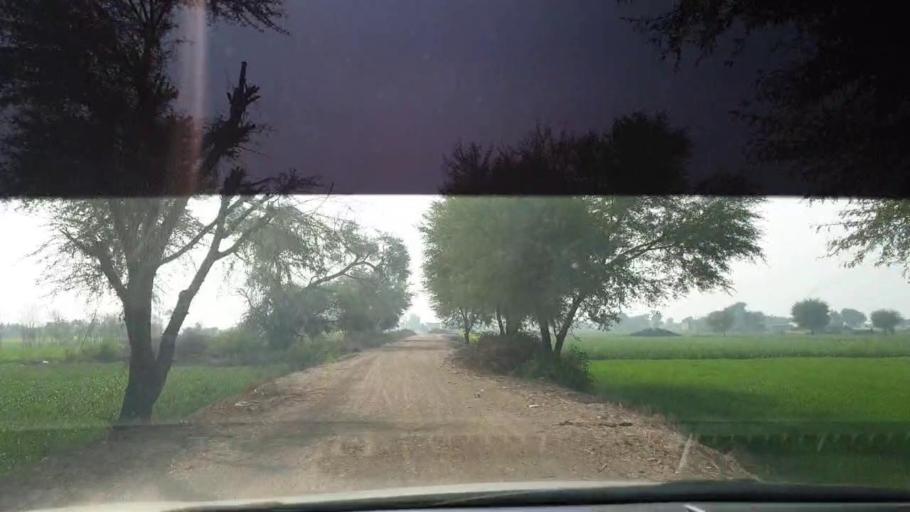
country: PK
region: Sindh
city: Berani
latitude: 25.7696
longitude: 68.7987
